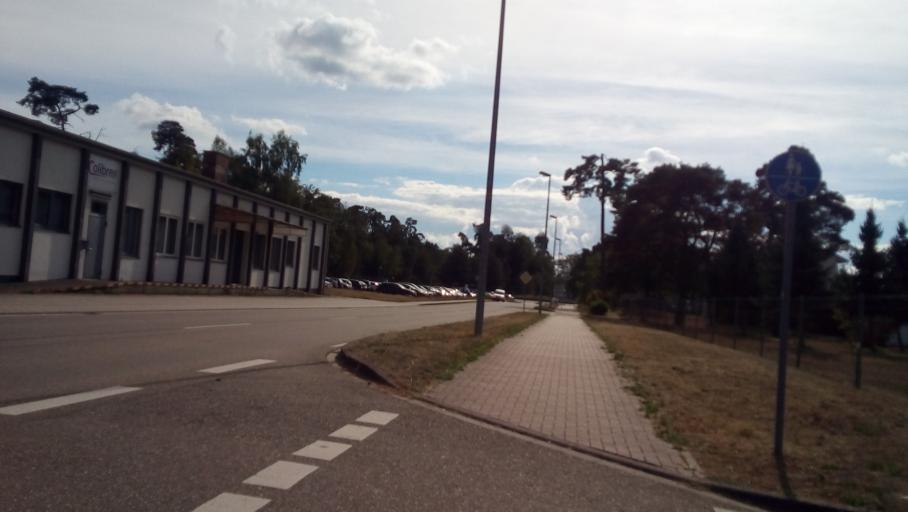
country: DE
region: Baden-Wuerttemberg
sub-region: Karlsruhe Region
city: Hugelsheim
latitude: 48.7809
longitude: 8.0966
